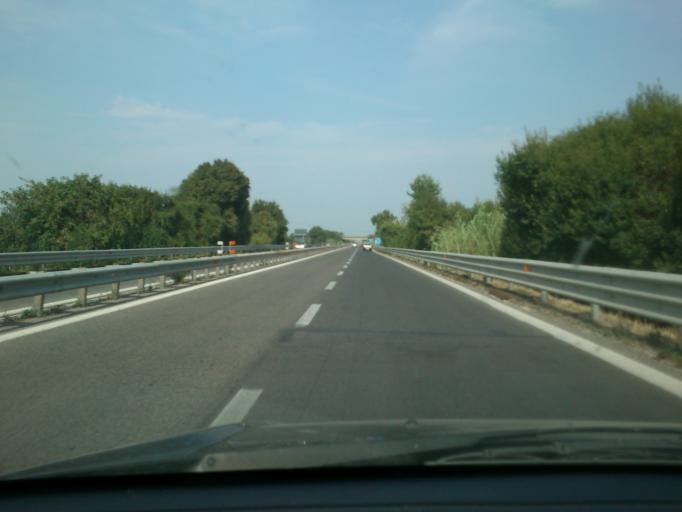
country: IT
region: The Marches
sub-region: Provincia di Pesaro e Urbino
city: Cuccurano
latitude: 43.7711
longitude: 12.9633
